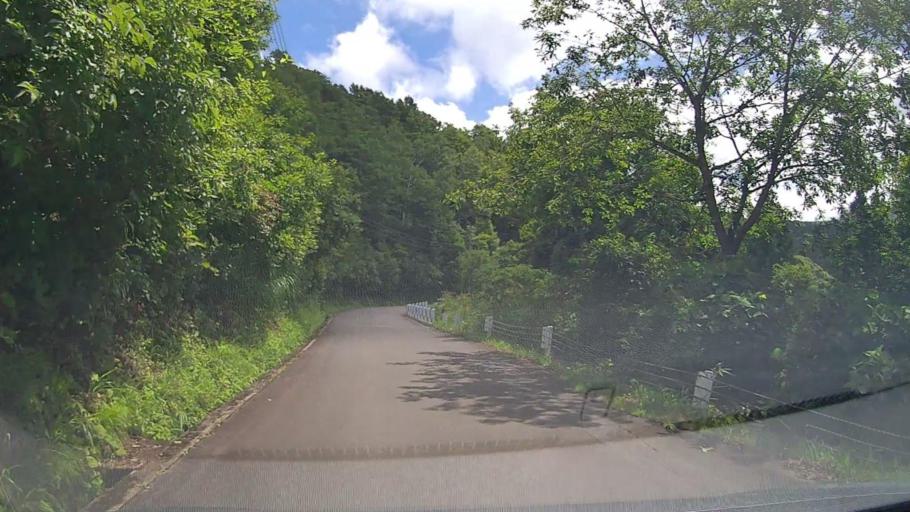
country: JP
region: Nagano
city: Iiyama
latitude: 36.9342
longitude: 138.4650
